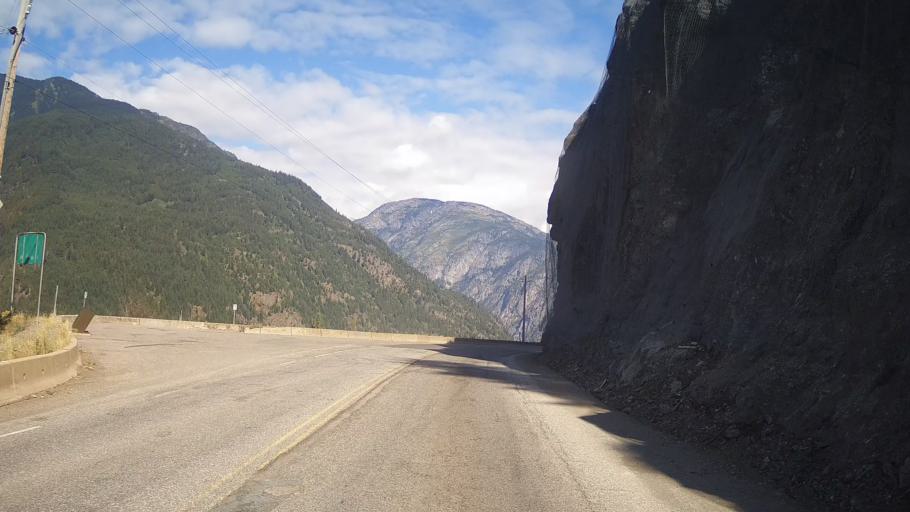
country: CA
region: British Columbia
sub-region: Thompson-Nicola Regional District
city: Ashcroft
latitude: 50.0772
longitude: -121.5490
